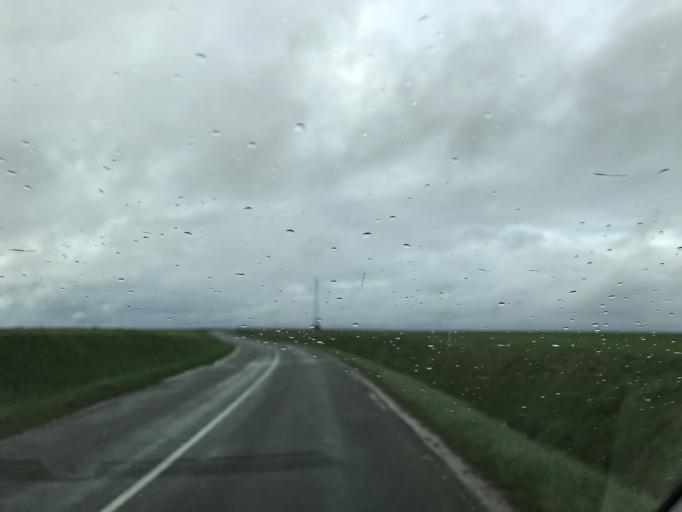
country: FR
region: Picardie
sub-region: Departement de l'Aisne
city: Billy-sur-Aisne
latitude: 49.3492
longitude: 3.3649
